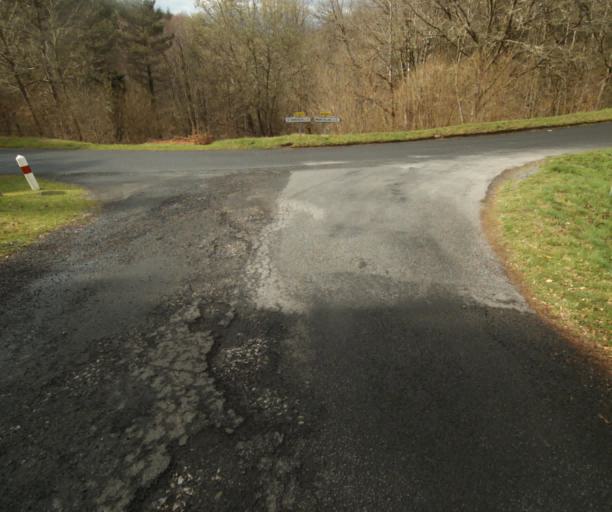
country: FR
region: Limousin
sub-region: Departement de la Correze
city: Saint-Privat
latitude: 45.2547
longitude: 1.9868
